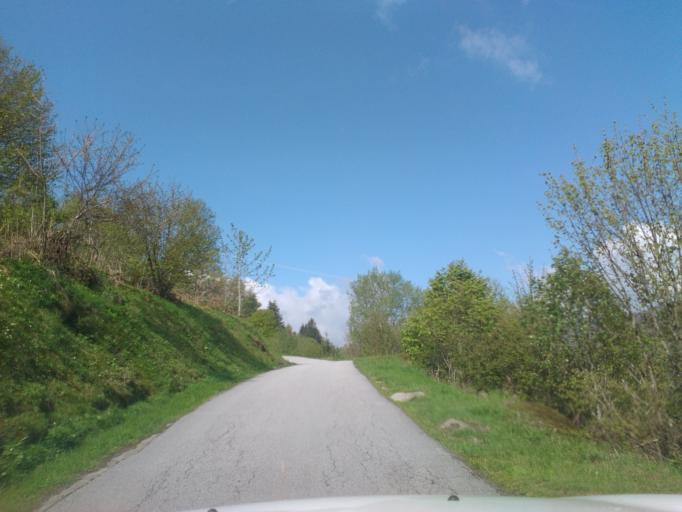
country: FR
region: Lorraine
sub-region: Departement des Vosges
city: Cornimont
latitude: 47.9853
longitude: 6.7978
